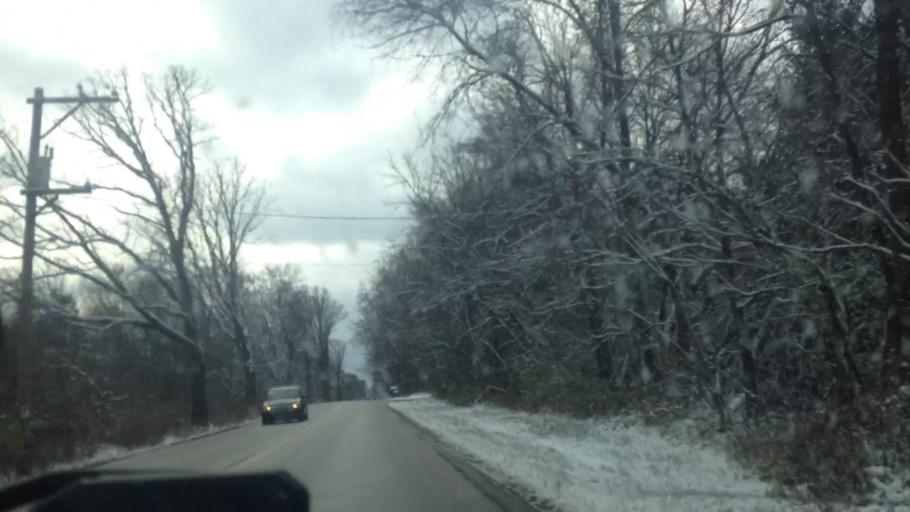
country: US
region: Wisconsin
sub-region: Waukesha County
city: Lannon
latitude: 43.1744
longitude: -88.1830
